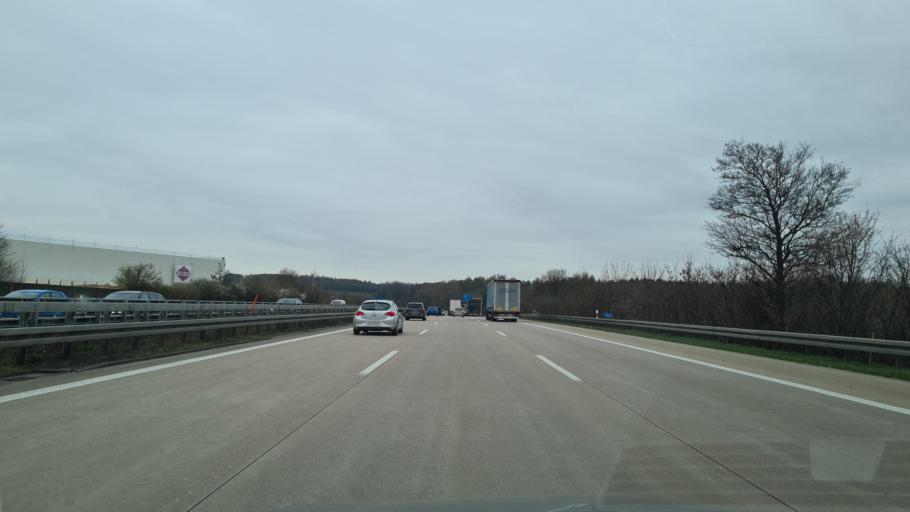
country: DE
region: Saxony
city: Hainichen
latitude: 50.9912
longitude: 13.1191
